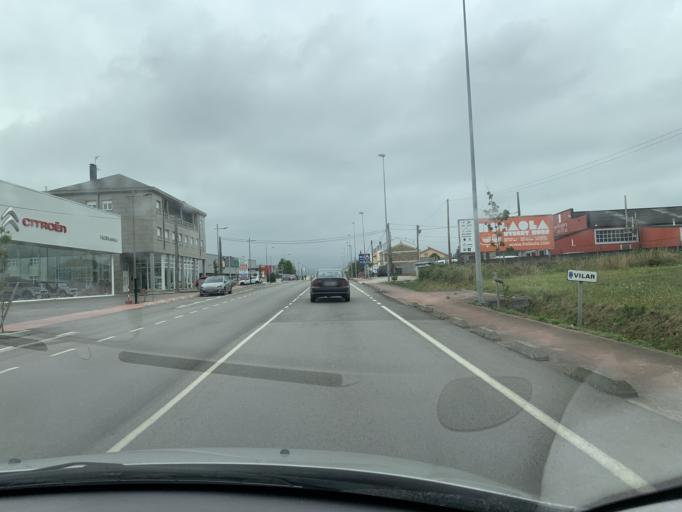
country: ES
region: Galicia
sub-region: Provincia de Lugo
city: Ribadeo
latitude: 43.5404
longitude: -7.0650
